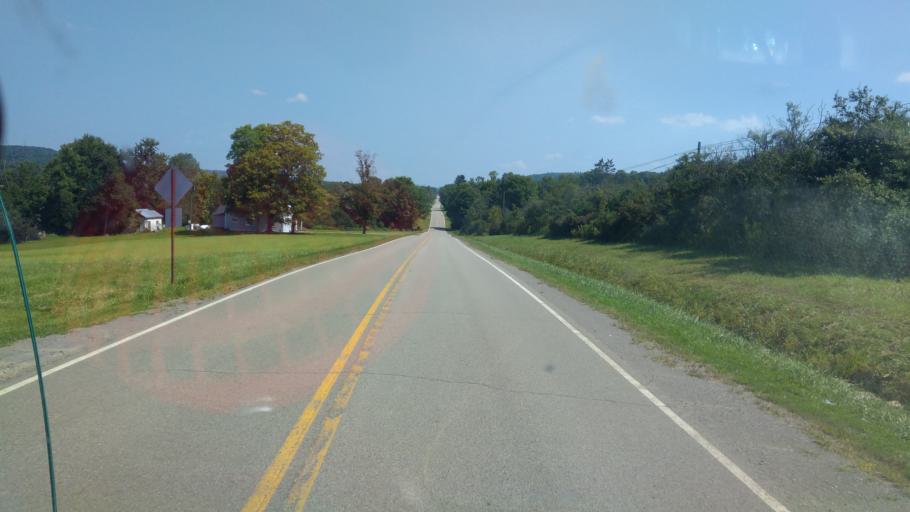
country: US
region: New York
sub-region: Allegany County
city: Belmont
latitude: 42.2901
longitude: -77.9316
